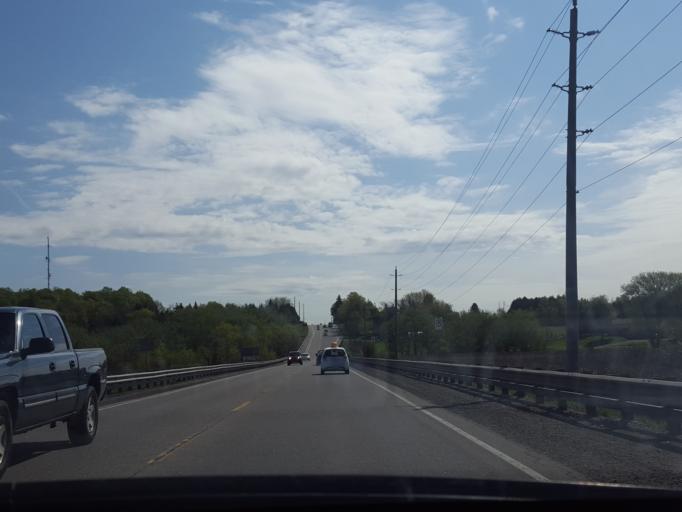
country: CA
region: Ontario
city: Uxbridge
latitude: 44.1032
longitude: -78.9291
